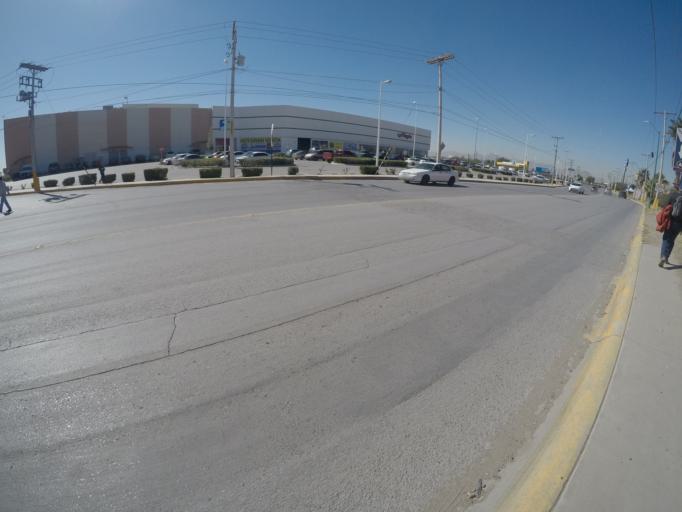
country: US
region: Texas
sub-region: El Paso County
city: Socorro
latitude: 31.6950
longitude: -106.3786
